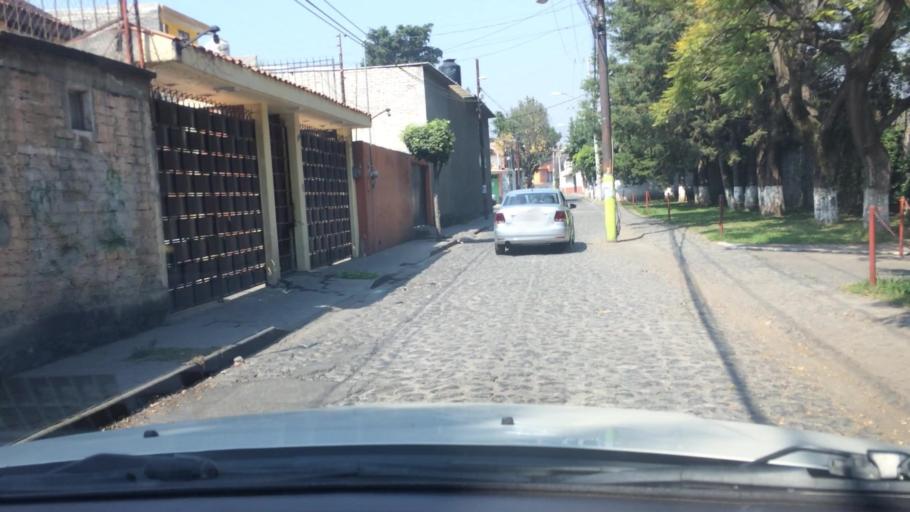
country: MX
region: Mexico City
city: Xochimilco
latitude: 19.2637
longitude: -99.1344
